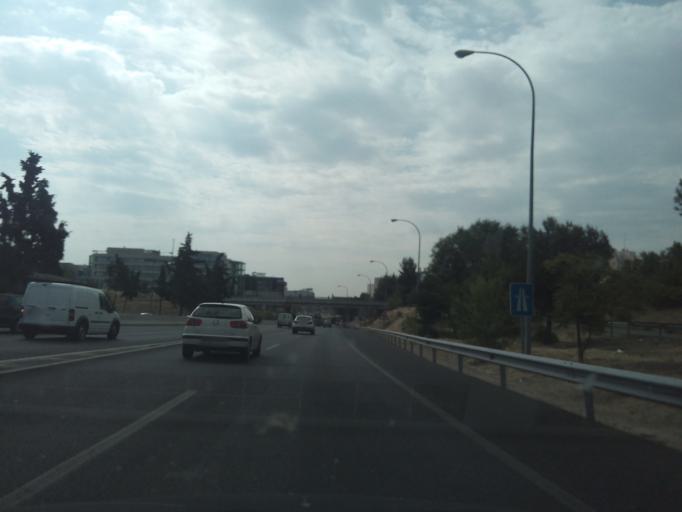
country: ES
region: Madrid
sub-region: Provincia de Madrid
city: Hortaleza
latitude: 40.4778
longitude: -3.6396
